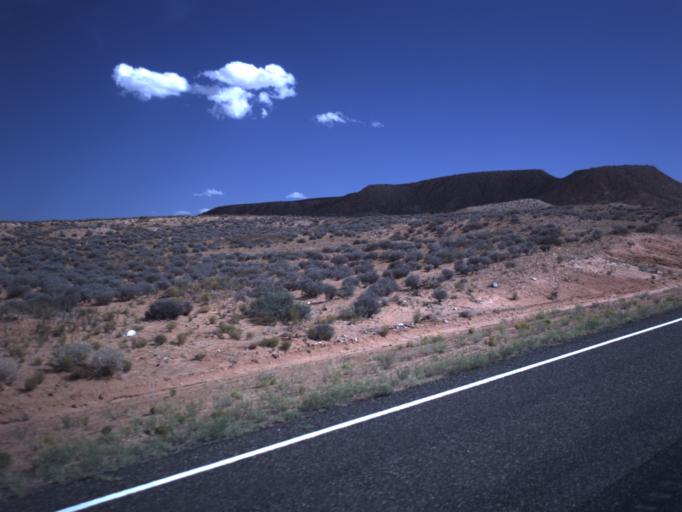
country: US
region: Utah
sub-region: Wayne County
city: Loa
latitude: 38.1554
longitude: -110.6211
